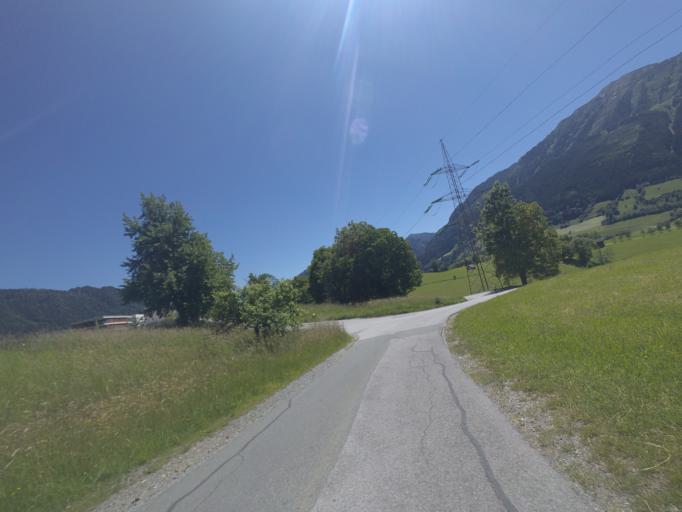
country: AT
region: Salzburg
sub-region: Politischer Bezirk Sankt Johann im Pongau
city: Schwarzach im Pongau
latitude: 47.3226
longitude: 13.1361
